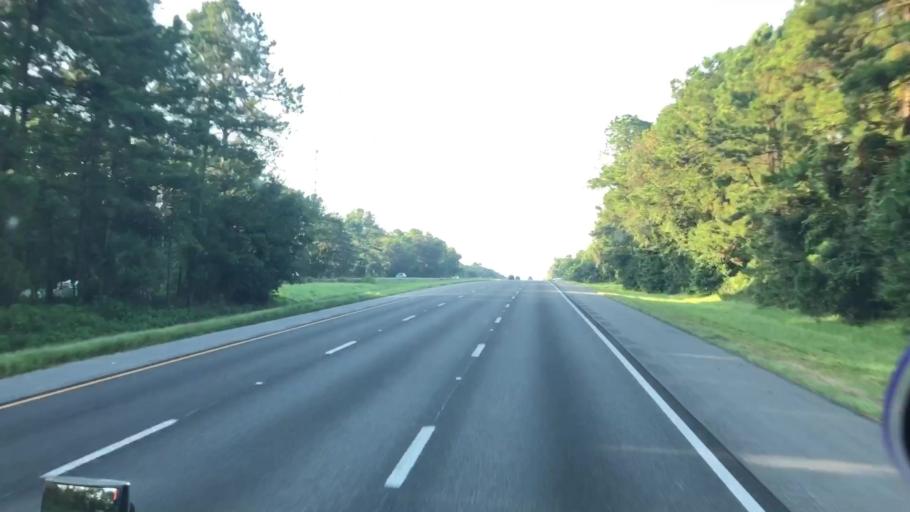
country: US
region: Florida
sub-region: Marion County
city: Citra
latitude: 29.3516
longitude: -82.2206
